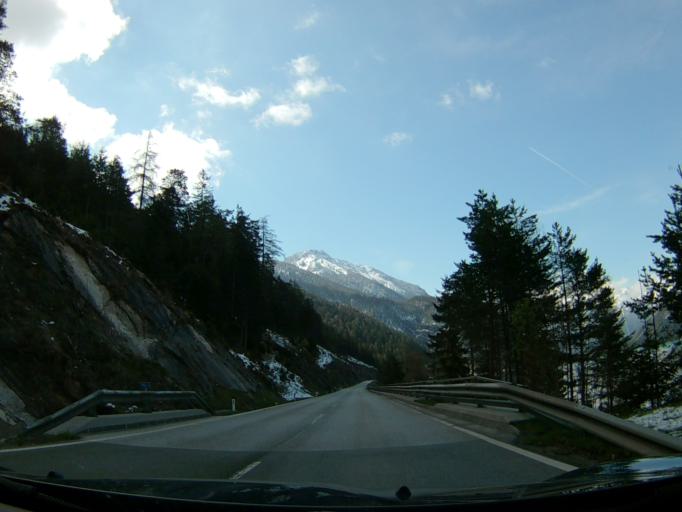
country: AT
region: Tyrol
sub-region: Politischer Bezirk Schwaz
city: Achenkirch
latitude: 47.4956
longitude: 11.7121
